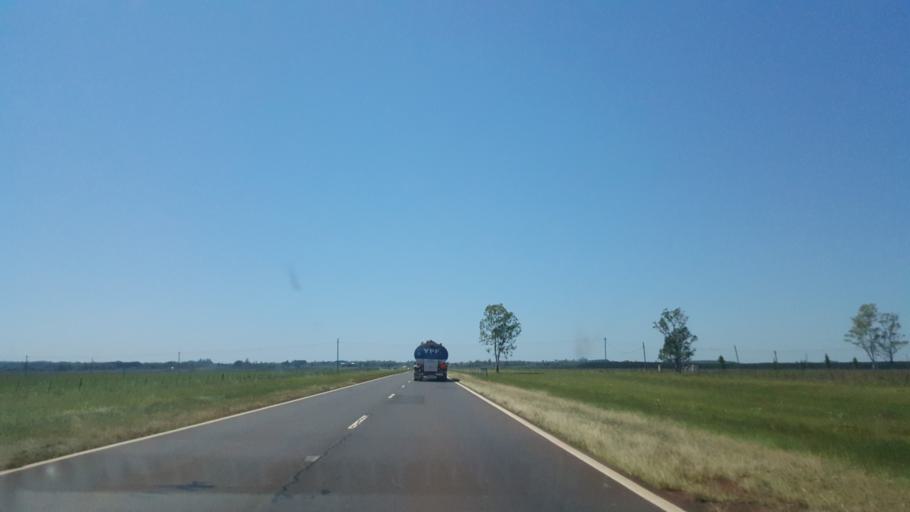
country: AR
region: Corrientes
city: Santo Tome
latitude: -28.5231
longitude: -56.1053
